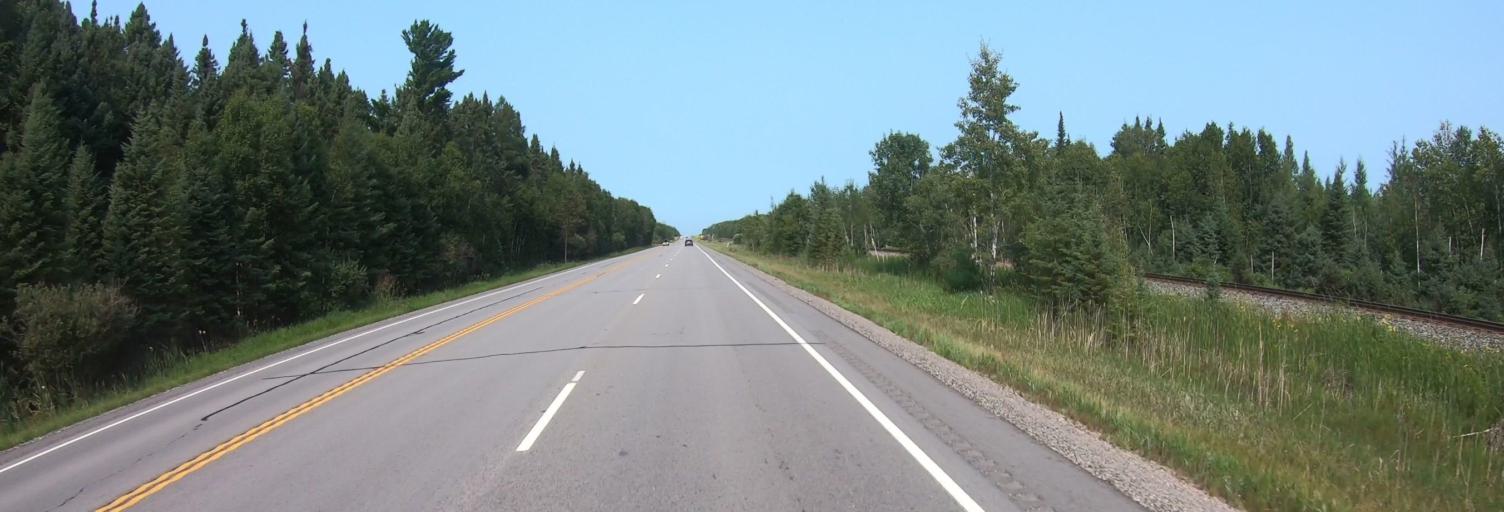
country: CA
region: Ontario
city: Fort Frances
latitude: 48.4540
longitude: -93.2760
